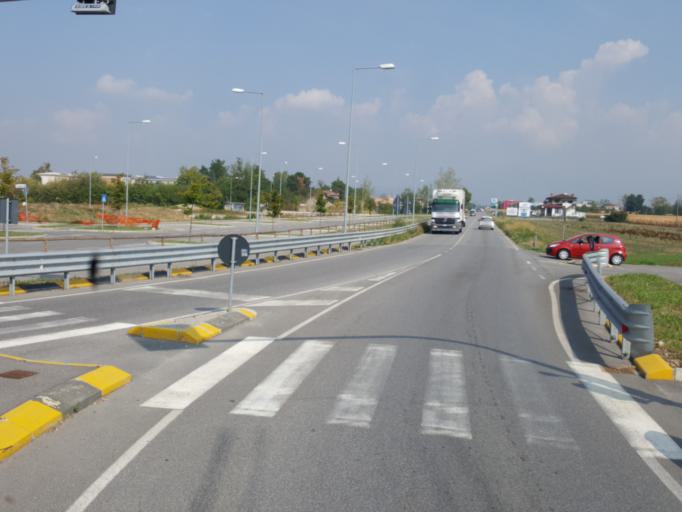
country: IT
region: Lombardy
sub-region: Provincia di Bergamo
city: Calcinate
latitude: 45.6199
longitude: 9.8075
